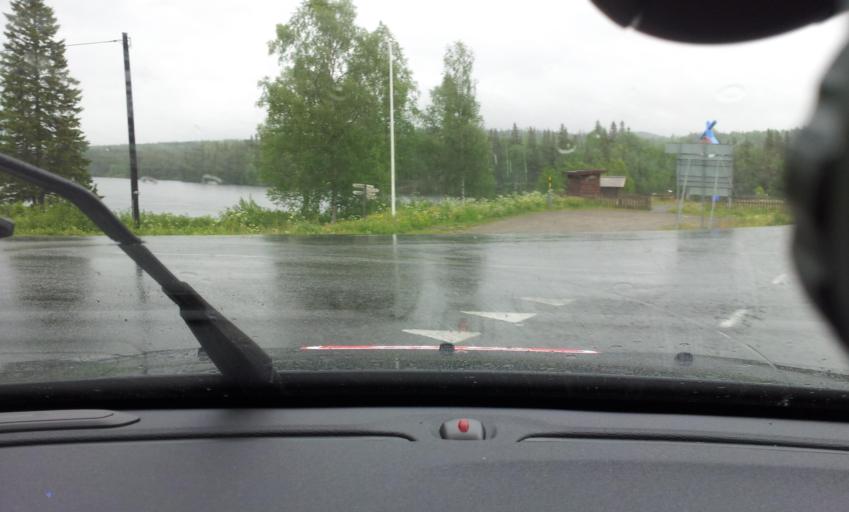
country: SE
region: Jaemtland
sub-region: Are Kommun
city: Are
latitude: 63.3108
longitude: 13.2301
